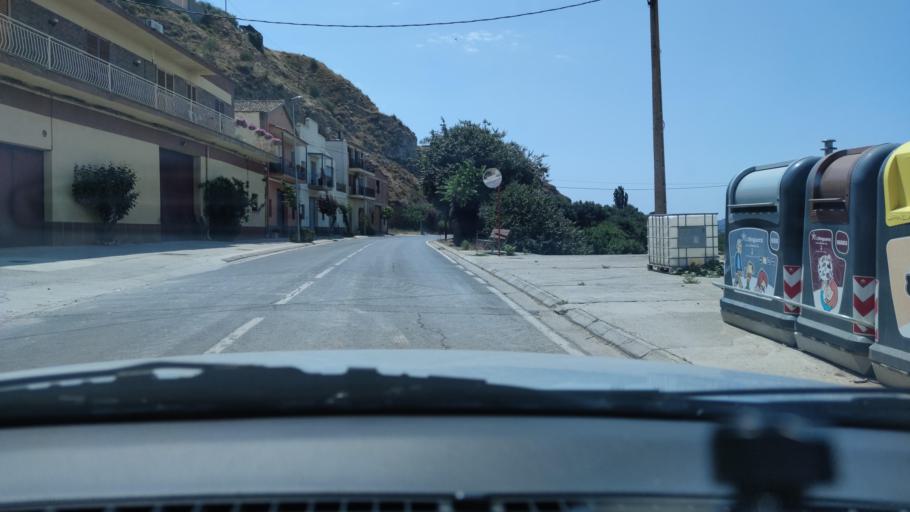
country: ES
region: Catalonia
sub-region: Provincia de Lleida
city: Alfarras
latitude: 41.8492
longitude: 0.5853
